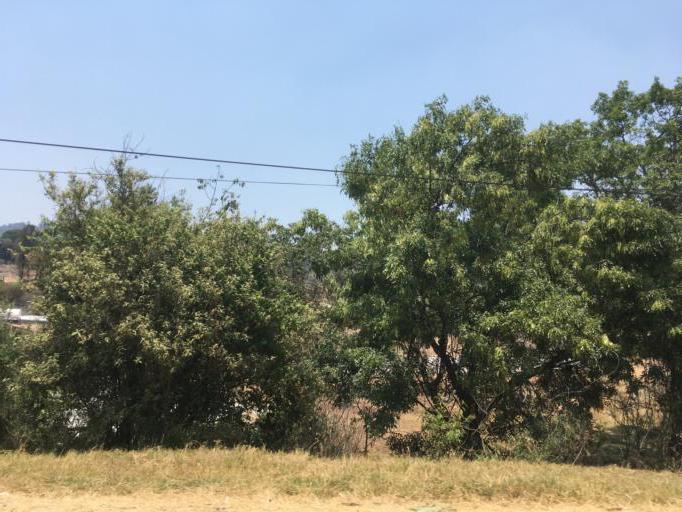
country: MX
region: Michoacan
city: Quiroga
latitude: 19.6591
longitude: -101.5086
